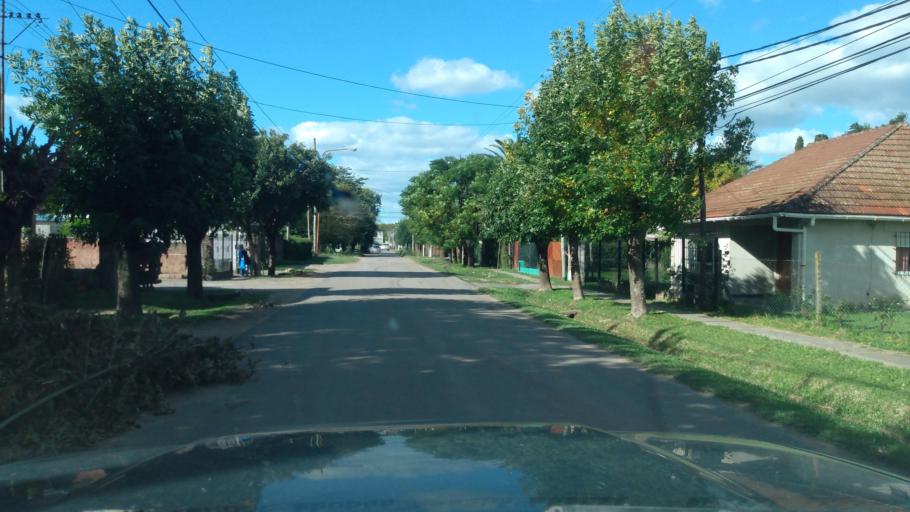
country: AR
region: Buenos Aires
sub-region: Partido de Lujan
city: Lujan
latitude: -34.5829
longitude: -59.0946
